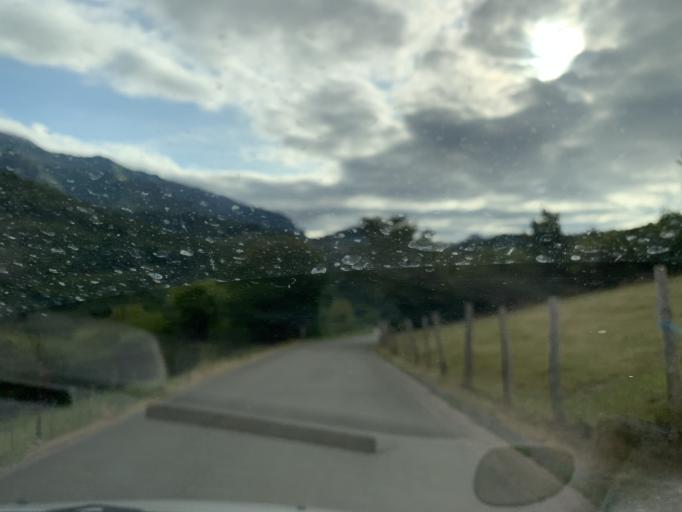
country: ES
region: Asturias
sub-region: Province of Asturias
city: Carrena
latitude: 43.3181
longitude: -4.8493
